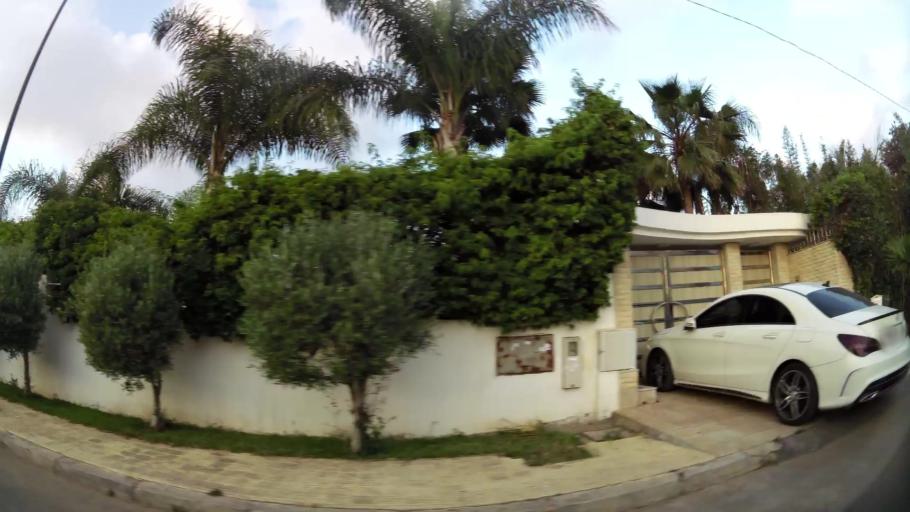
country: MA
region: Rabat-Sale-Zemmour-Zaer
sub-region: Rabat
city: Rabat
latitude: 33.9693
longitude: -6.8319
